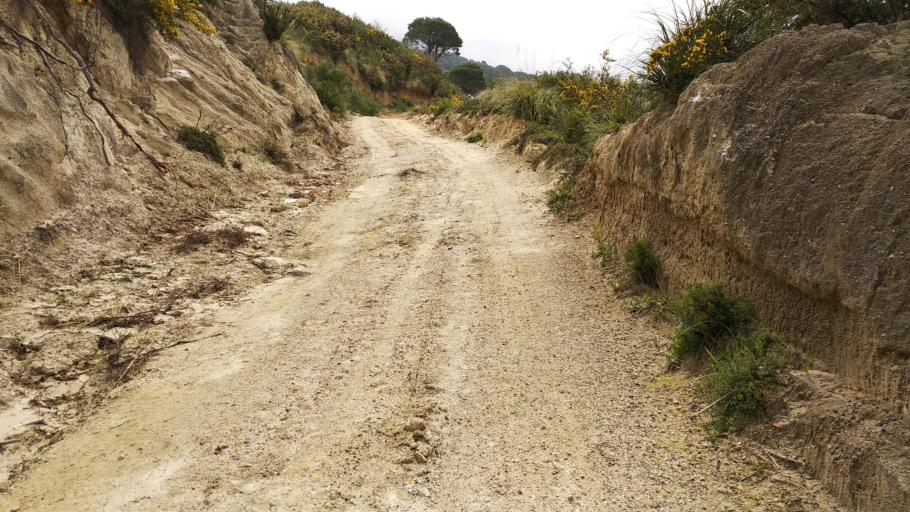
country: IT
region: Sicily
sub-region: Messina
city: Saponara
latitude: 38.2100
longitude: 15.4804
